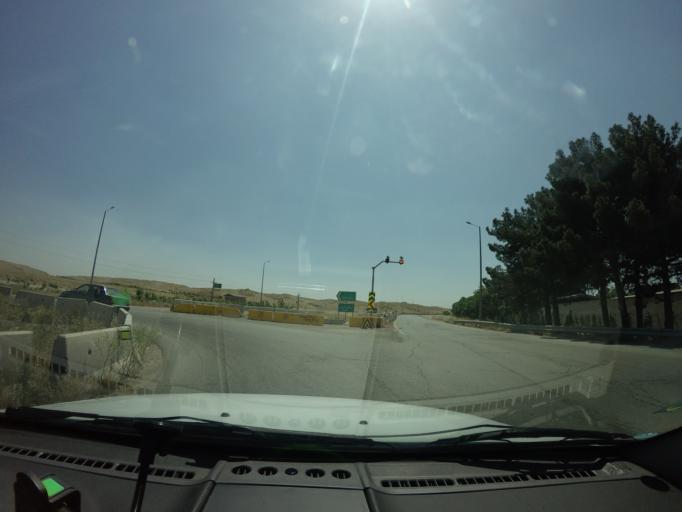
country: IR
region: Tehran
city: Eslamshahr
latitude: 35.4369
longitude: 51.2074
